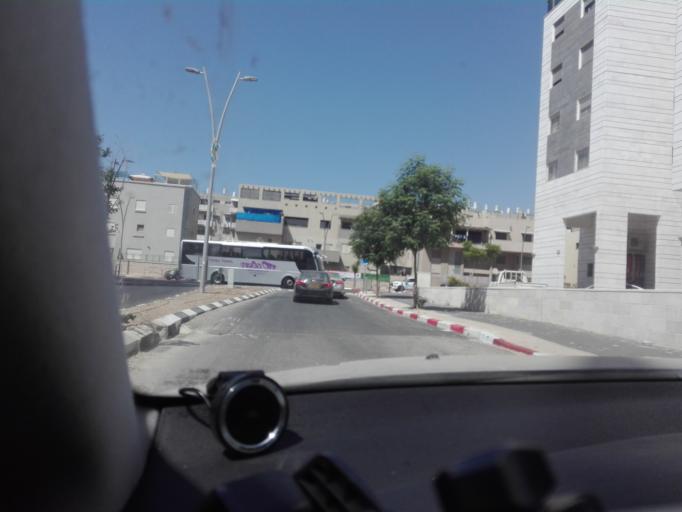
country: IL
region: Central District
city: Bene 'Ayish
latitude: 31.7269
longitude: 34.7393
